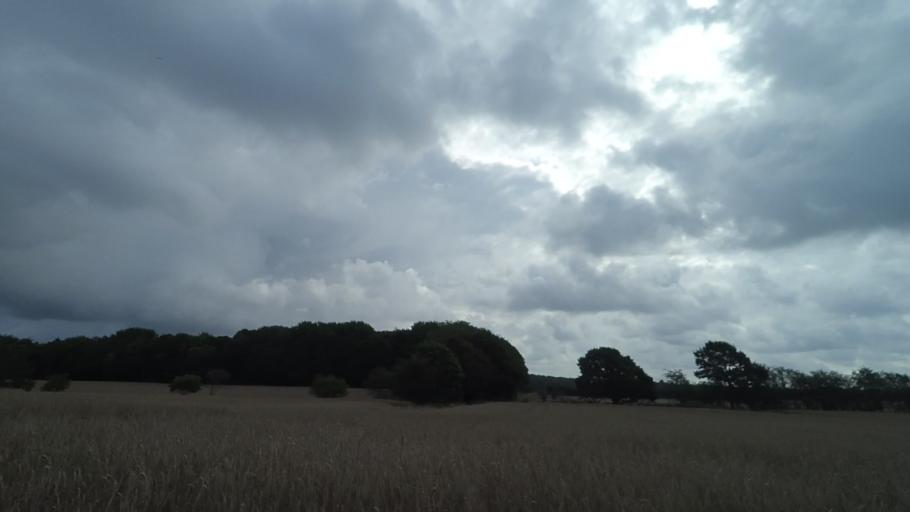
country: DK
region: Central Jutland
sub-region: Syddjurs Kommune
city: Ryomgard
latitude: 56.4458
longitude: 10.5597
